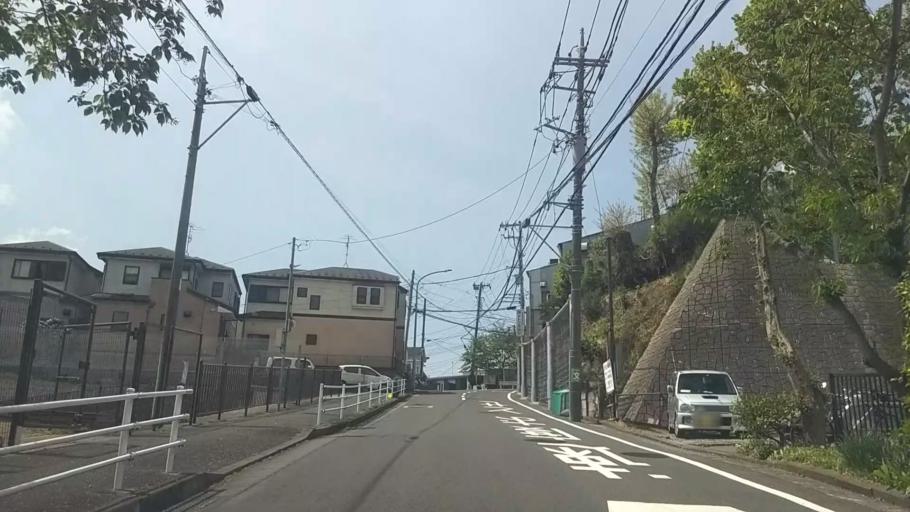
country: JP
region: Kanagawa
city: Yokohama
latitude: 35.3938
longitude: 139.5934
